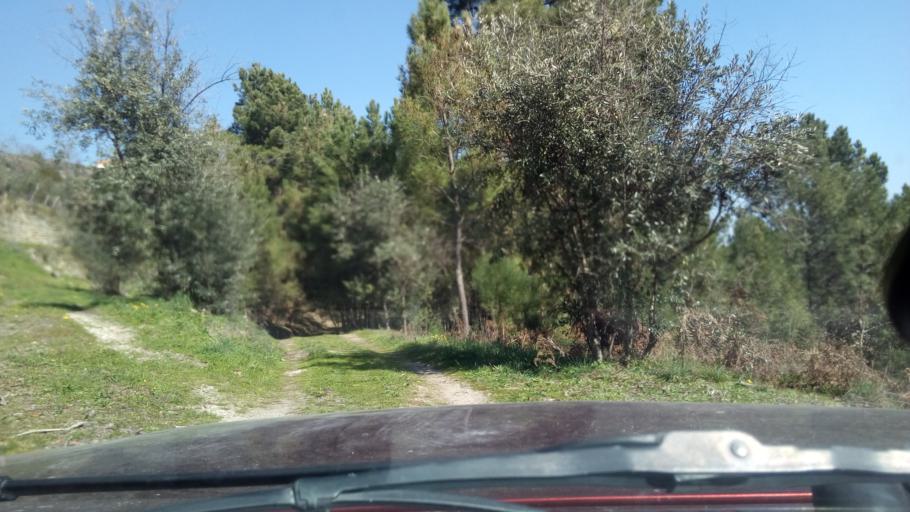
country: PT
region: Guarda
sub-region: Fornos de Algodres
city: Fornos de Algodres
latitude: 40.6261
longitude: -7.5369
